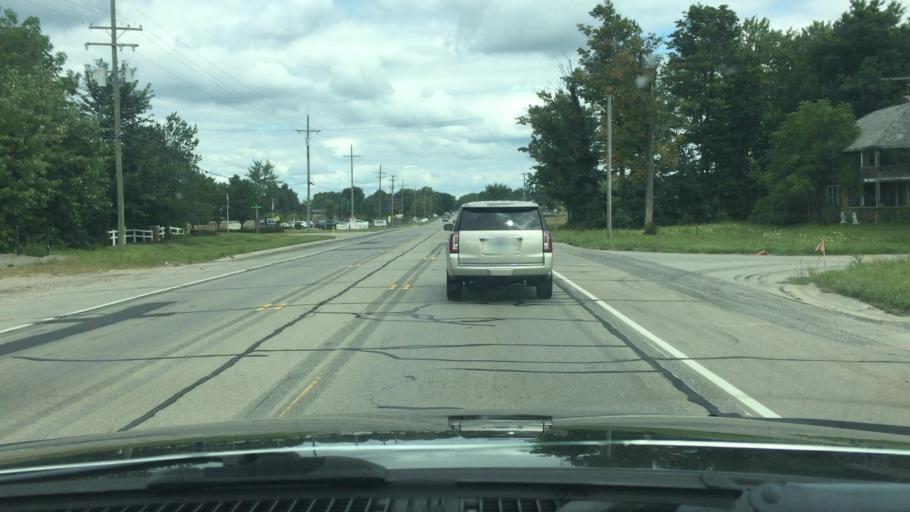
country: US
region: Michigan
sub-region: Lapeer County
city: Almont
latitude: 42.9009
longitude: -83.0440
